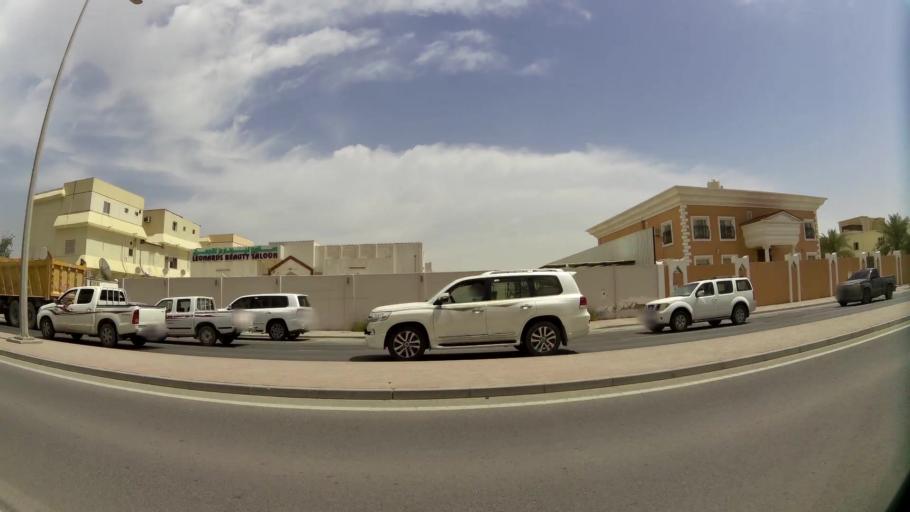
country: QA
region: Baladiyat ar Rayyan
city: Ar Rayyan
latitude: 25.2758
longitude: 51.4202
